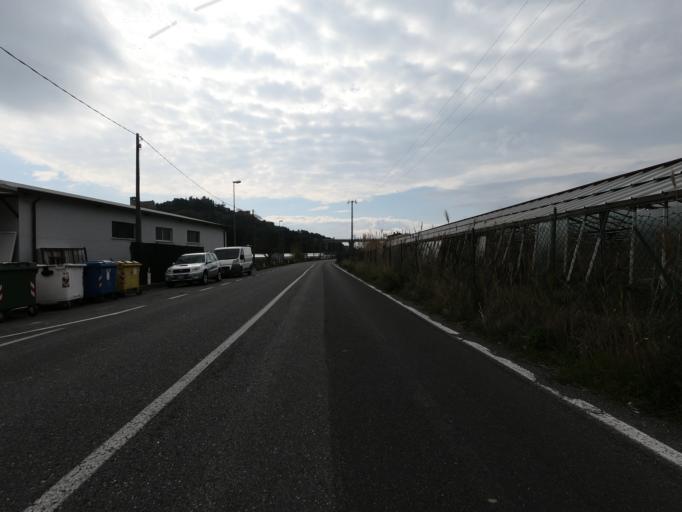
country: IT
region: Liguria
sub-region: Provincia di Savona
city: Andora
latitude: 43.9696
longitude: 8.1403
